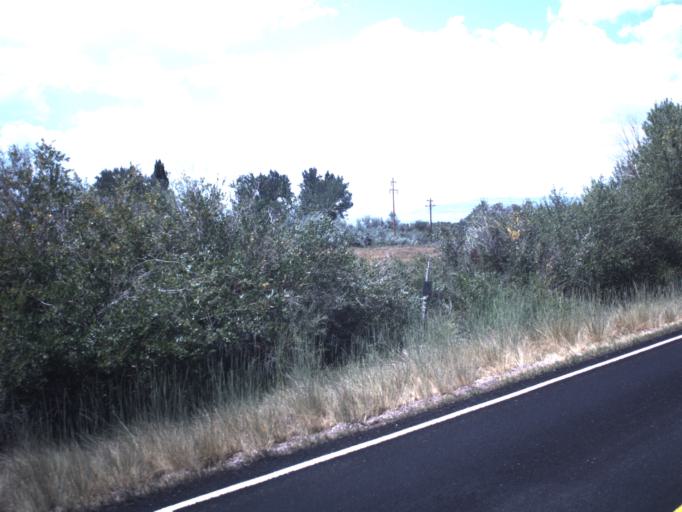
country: US
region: Utah
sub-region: Duchesne County
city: Roosevelt
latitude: 40.4056
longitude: -109.9163
